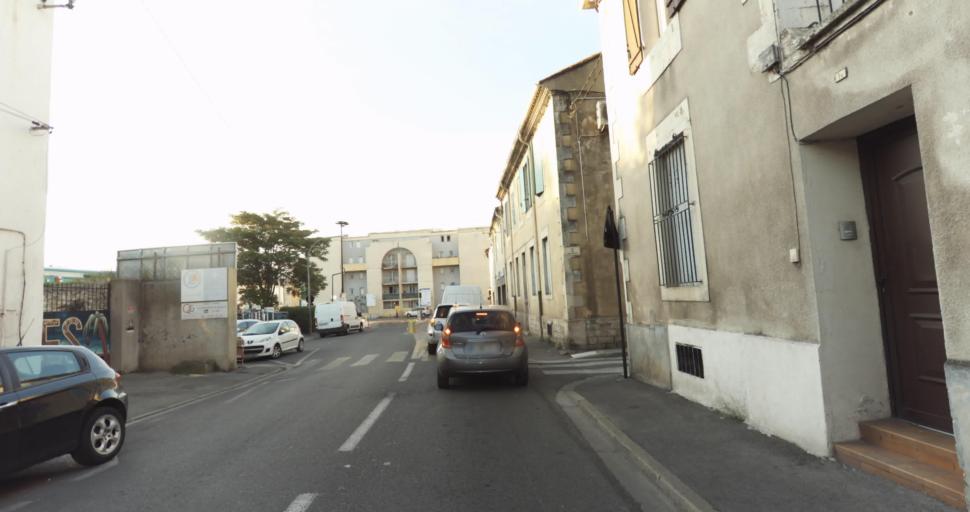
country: FR
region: Languedoc-Roussillon
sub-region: Departement du Gard
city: Nimes
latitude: 43.8411
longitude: 4.3717
